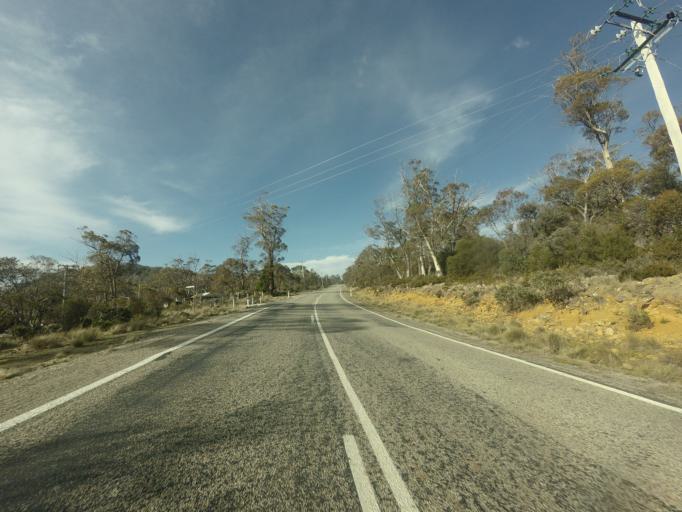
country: AU
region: Tasmania
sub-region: Meander Valley
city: Deloraine
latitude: -41.9903
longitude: 146.6915
